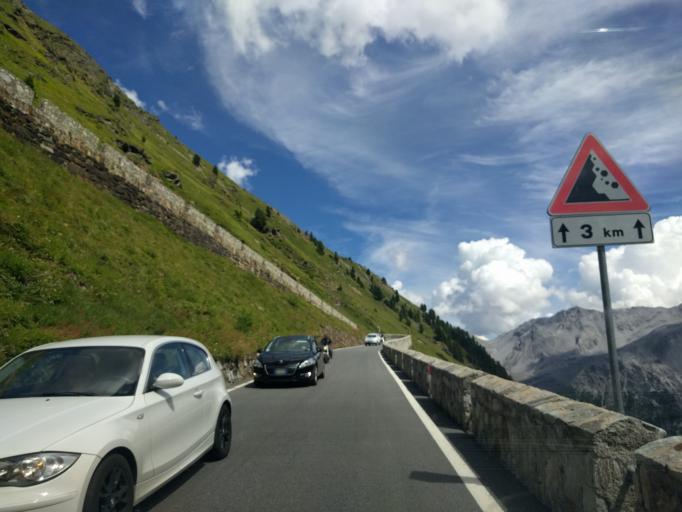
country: IT
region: Lombardy
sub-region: Provincia di Sondrio
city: Sant'Antonio
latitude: 46.5335
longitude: 10.4767
